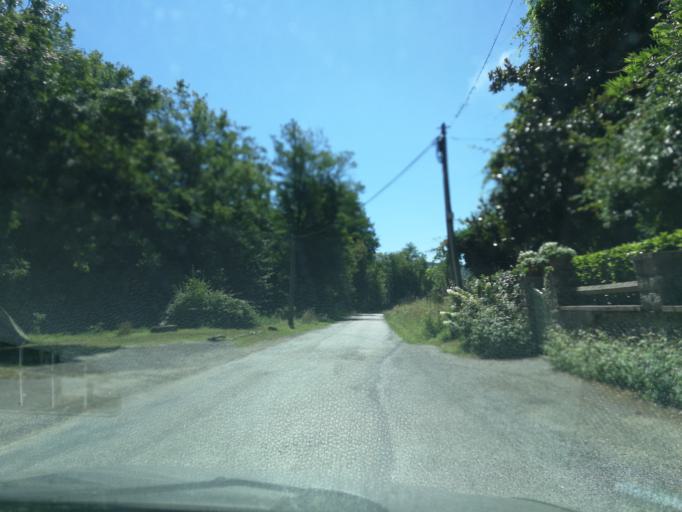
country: FR
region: Limousin
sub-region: Departement de la Correze
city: Argentat
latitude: 45.0932
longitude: 1.9245
